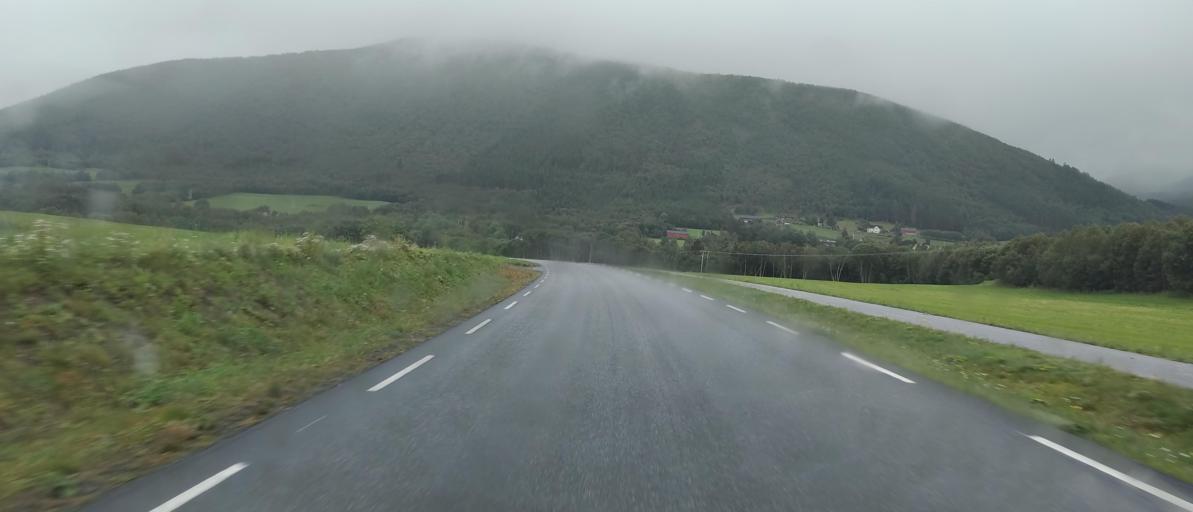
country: NO
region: More og Romsdal
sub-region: Eide
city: Eide
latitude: 62.8989
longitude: 7.4593
